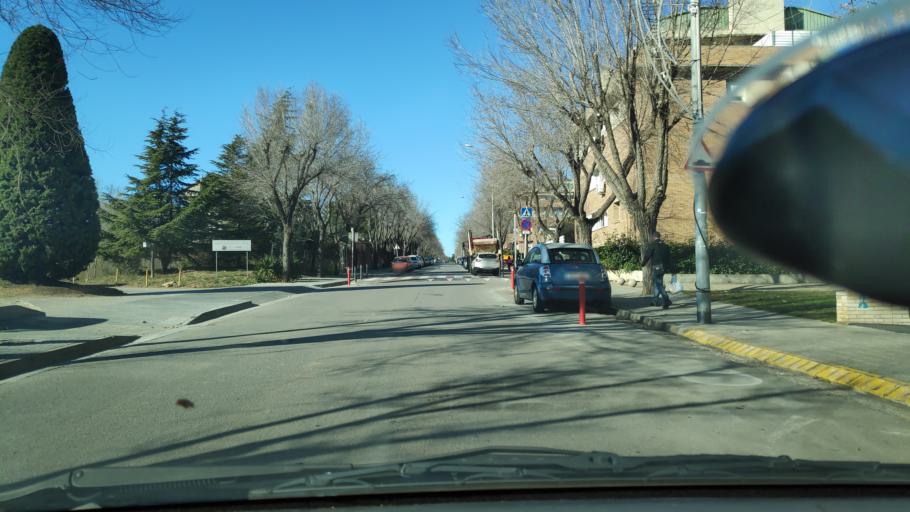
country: ES
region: Catalonia
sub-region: Provincia de Barcelona
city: Sant Quirze del Valles
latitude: 41.5350
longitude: 2.0722
